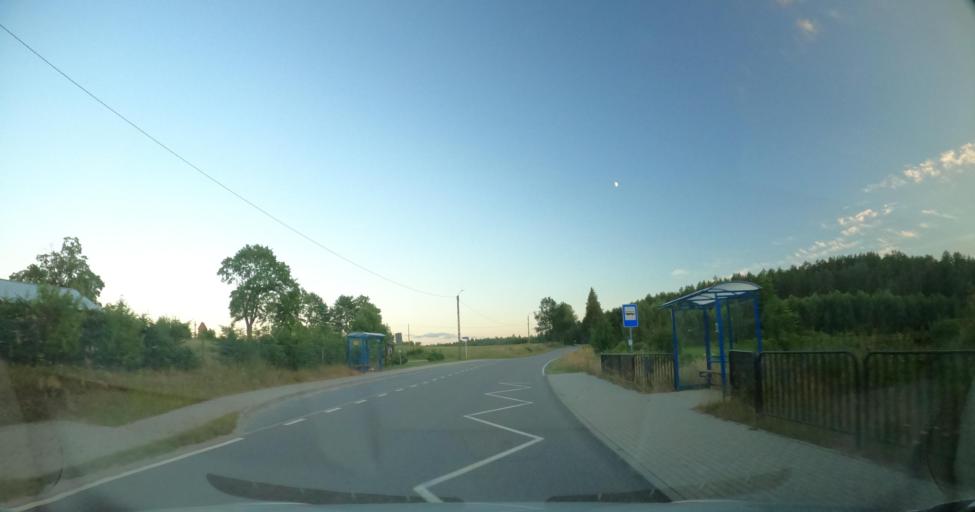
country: PL
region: Pomeranian Voivodeship
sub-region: Powiat wejherowski
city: Leczyce
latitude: 54.4972
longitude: 17.8423
